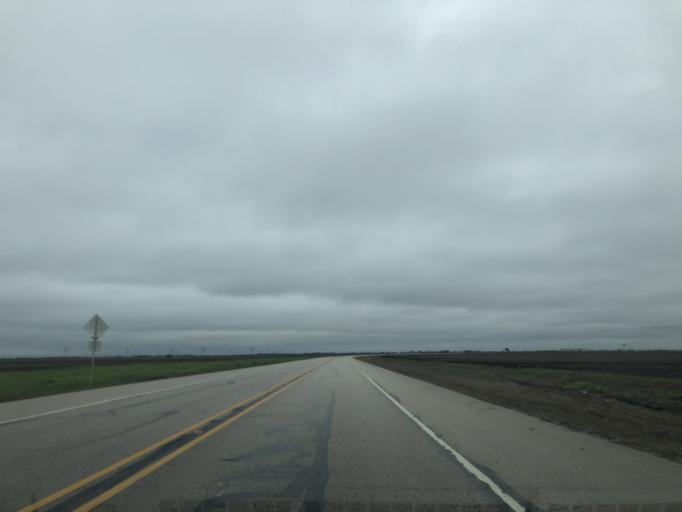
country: US
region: Texas
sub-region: Williamson County
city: Hutto
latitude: 30.5978
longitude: -97.5347
